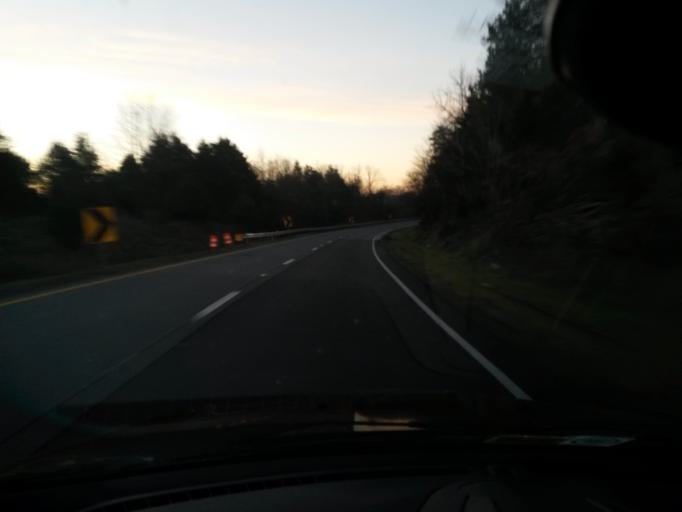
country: US
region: Virginia
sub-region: Botetourt County
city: Fincastle
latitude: 37.5804
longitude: -79.8322
